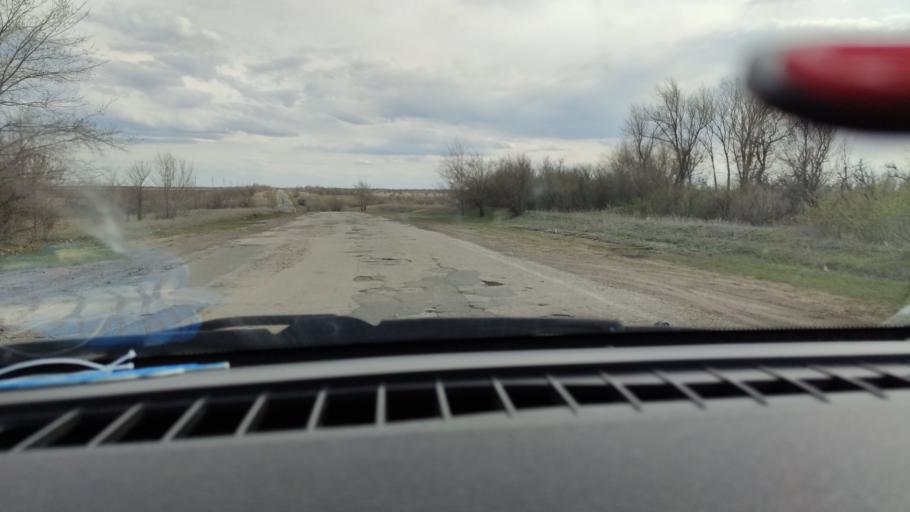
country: RU
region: Saratov
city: Rovnoye
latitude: 50.9594
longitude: 46.1190
